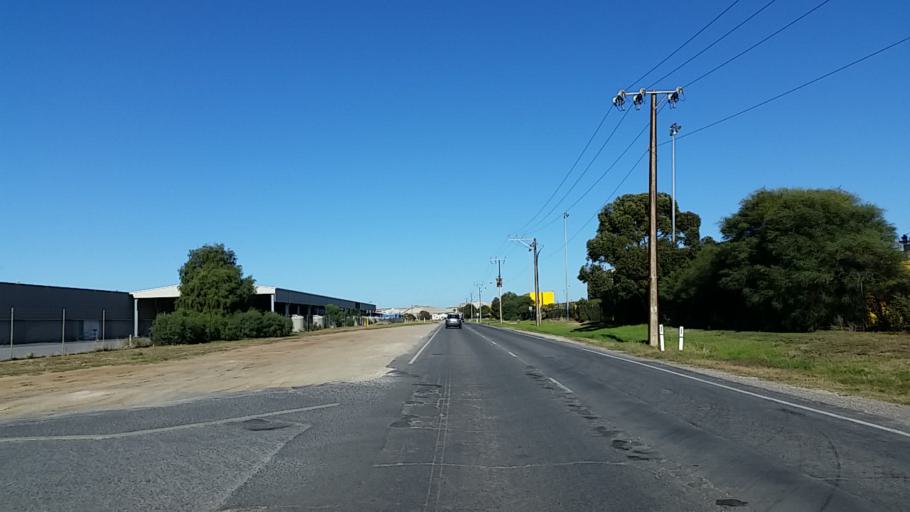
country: AU
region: South Australia
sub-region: Port Adelaide Enfield
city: Birkenhead
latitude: -34.8273
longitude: 138.5195
